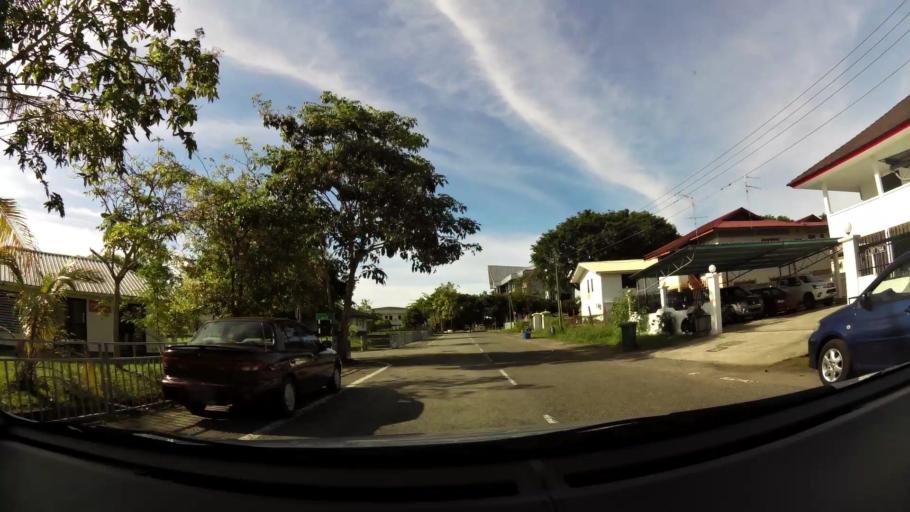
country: BN
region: Belait
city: Kuala Belait
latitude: 4.5859
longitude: 114.1938
